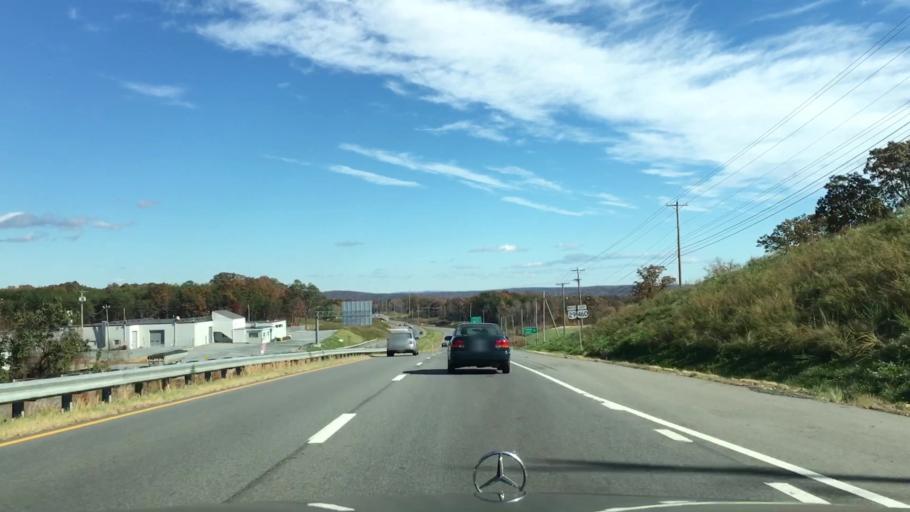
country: US
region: Virginia
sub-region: City of Lynchburg
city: Lynchburg
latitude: 37.3795
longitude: -79.1243
